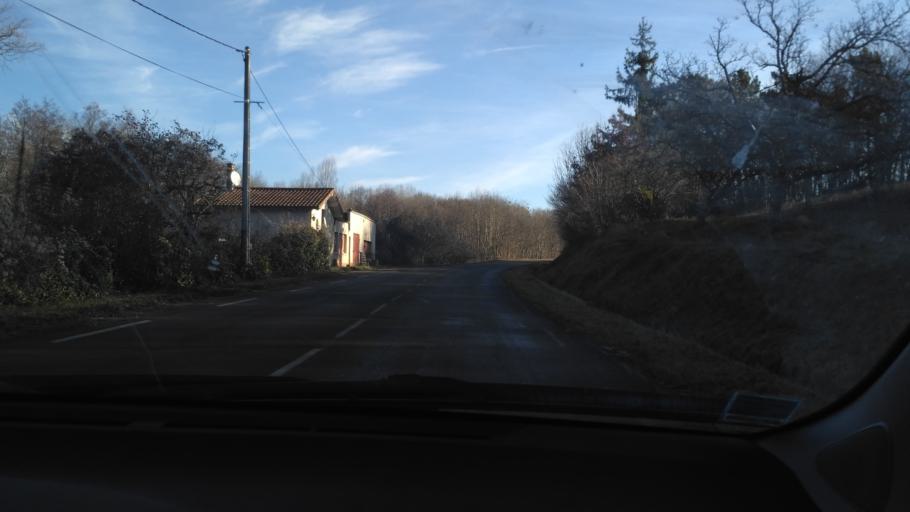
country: FR
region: Rhone-Alpes
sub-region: Departement de l'Isere
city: Saint-Antoine-l'Abbaye
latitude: 45.1588
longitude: 5.1696
